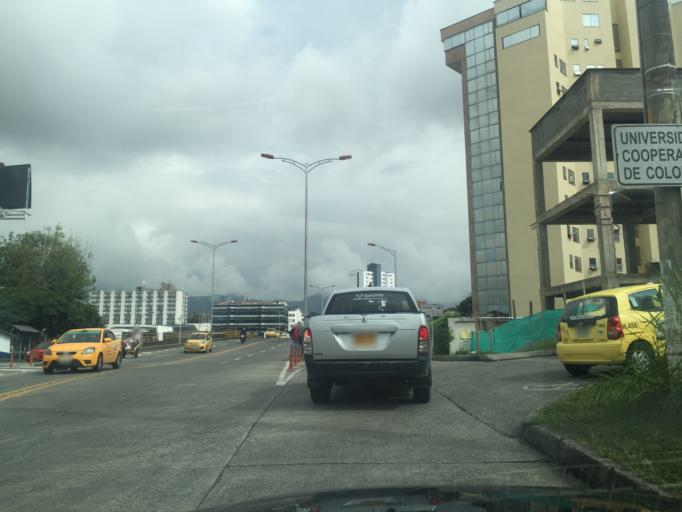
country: CO
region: Risaralda
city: Pereira
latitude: 4.8046
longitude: -75.6911
